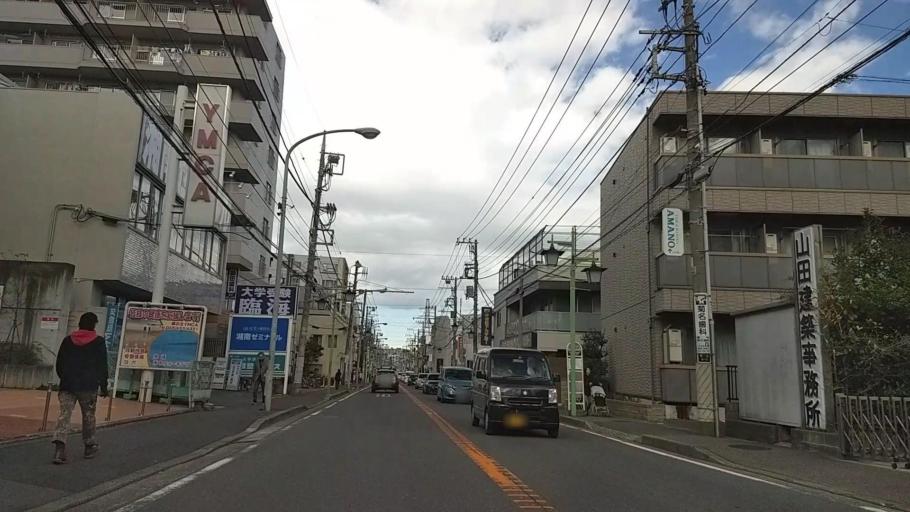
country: JP
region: Kanagawa
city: Yokohama
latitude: 35.5117
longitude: 139.6318
